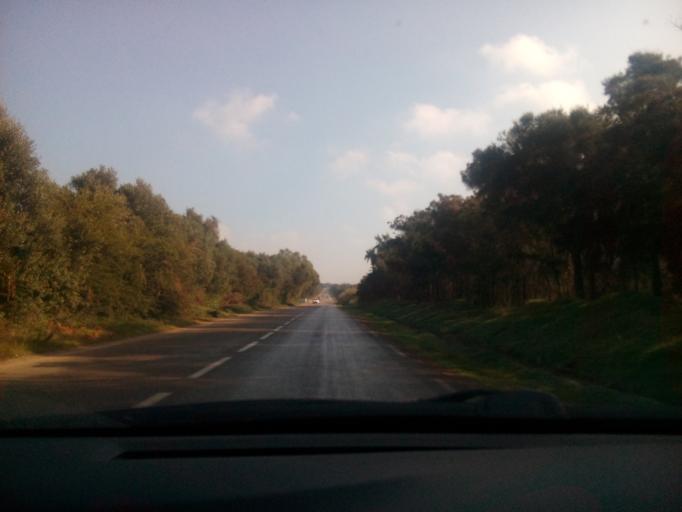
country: DZ
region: Oran
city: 'Ain el Turk
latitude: 35.7029
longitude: -0.8505
